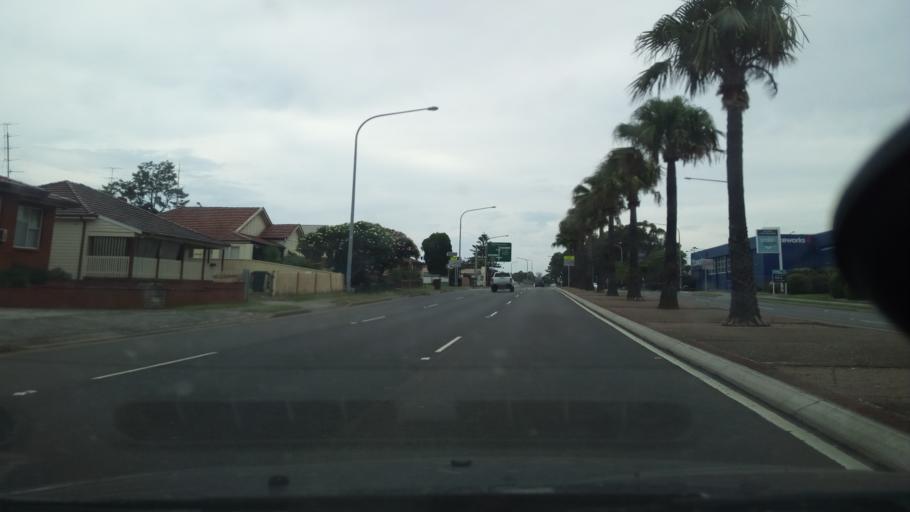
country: AU
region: New South Wales
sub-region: Wollongong
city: Fairy Meadow
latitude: -34.4040
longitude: 150.8911
